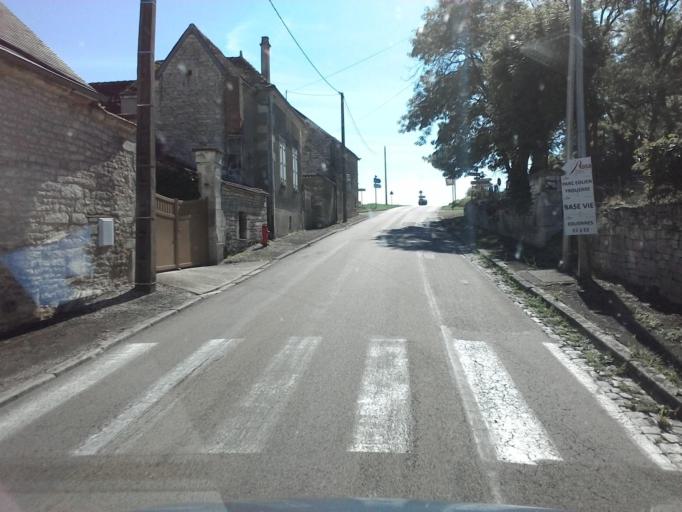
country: FR
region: Bourgogne
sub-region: Departement de l'Yonne
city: Tonnerre
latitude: 47.7905
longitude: 3.9469
